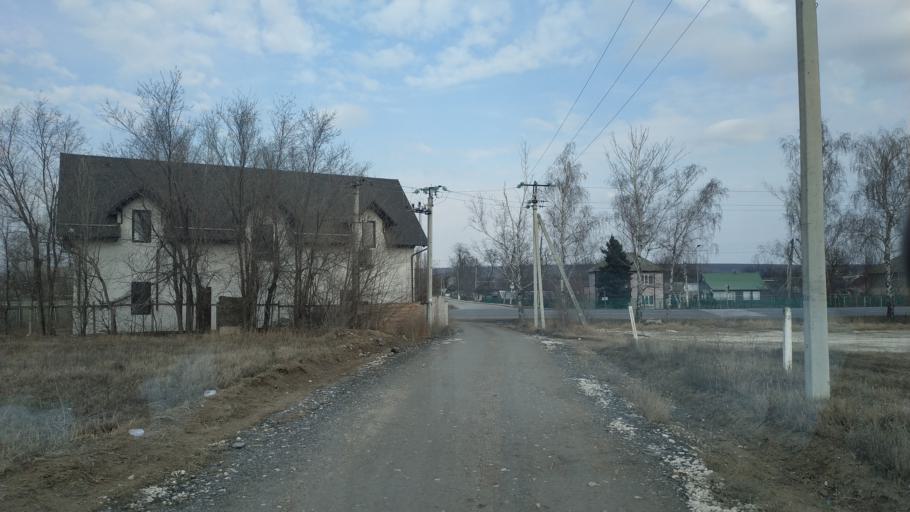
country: MD
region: Anenii Noi
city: Anenii Noi
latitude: 46.8990
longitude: 29.1335
